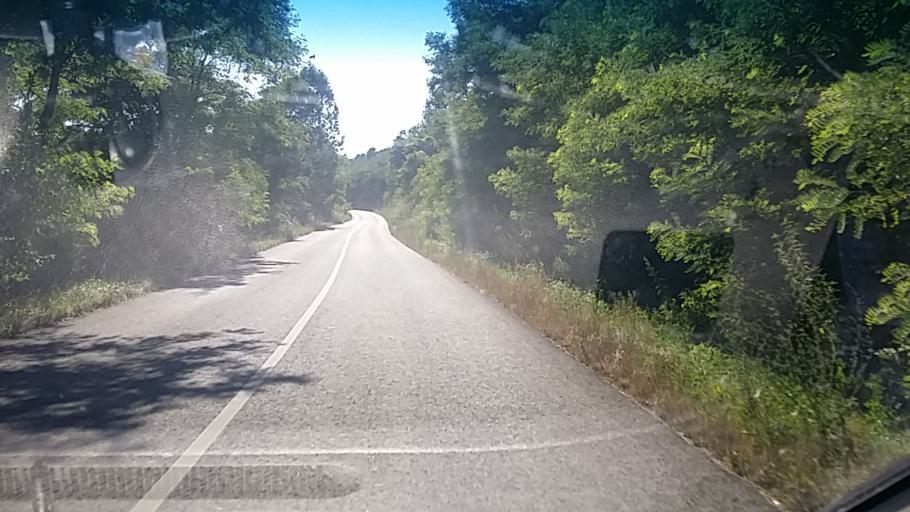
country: HU
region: Nograd
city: Romhany
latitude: 47.9226
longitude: 19.2079
